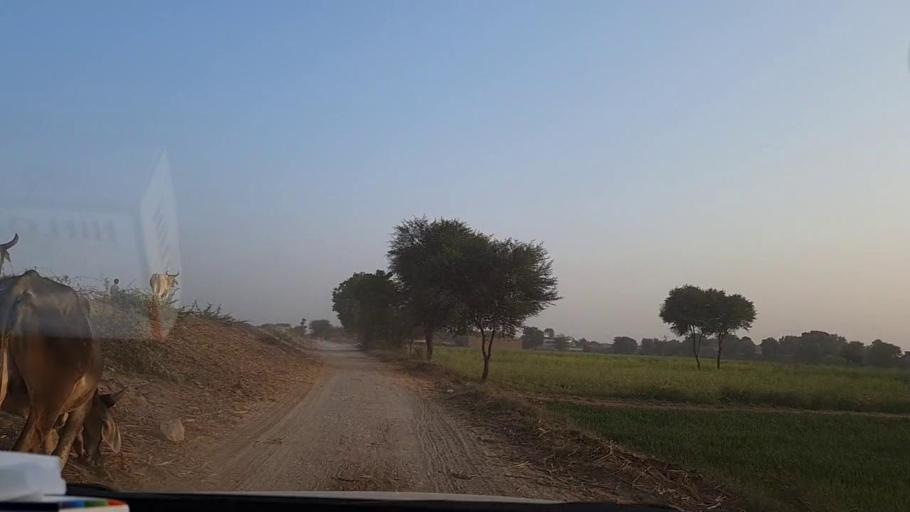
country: PK
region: Sindh
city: Tando Ghulam Ali
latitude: 25.1775
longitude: 68.9254
